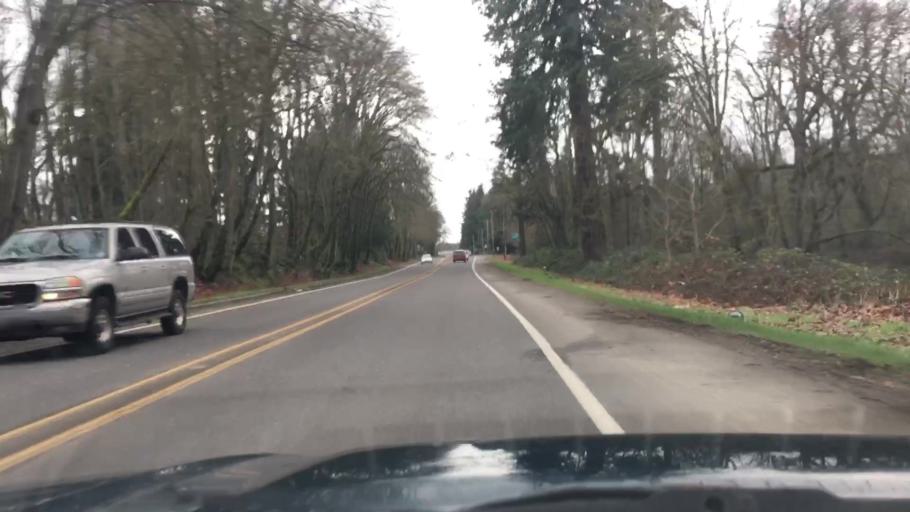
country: US
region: Oregon
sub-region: Lane County
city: Coburg
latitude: 44.1096
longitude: -123.0498
